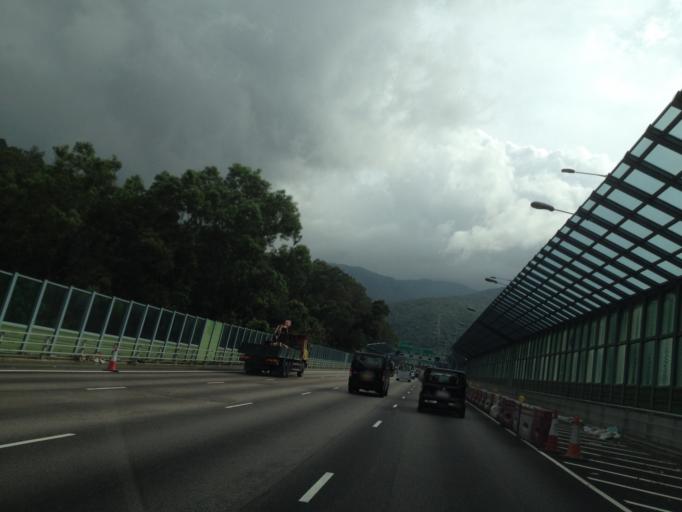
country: HK
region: Tai Po
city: Tai Po
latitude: 22.4426
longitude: 114.1713
